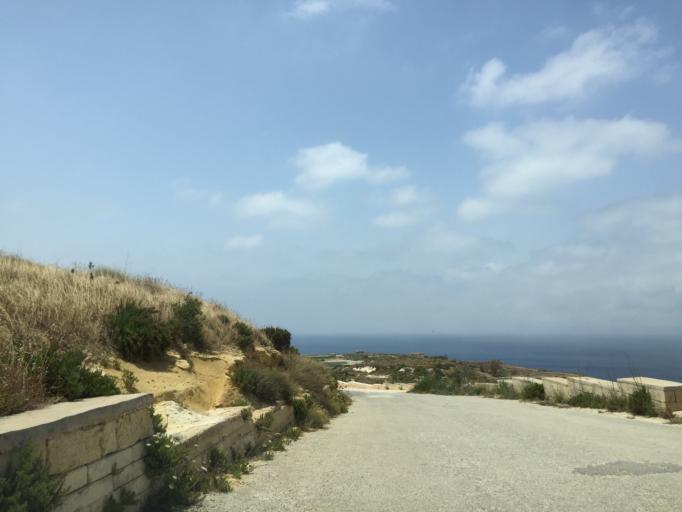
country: MT
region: L-Imgarr
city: Imgarr
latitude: 35.9028
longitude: 14.3359
